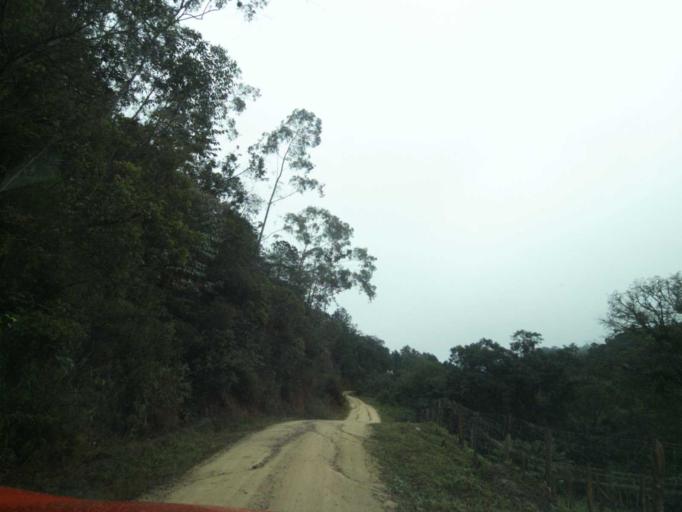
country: BR
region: Santa Catarina
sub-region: Anitapolis
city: Anitapolis
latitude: -27.9208
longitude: -49.1930
